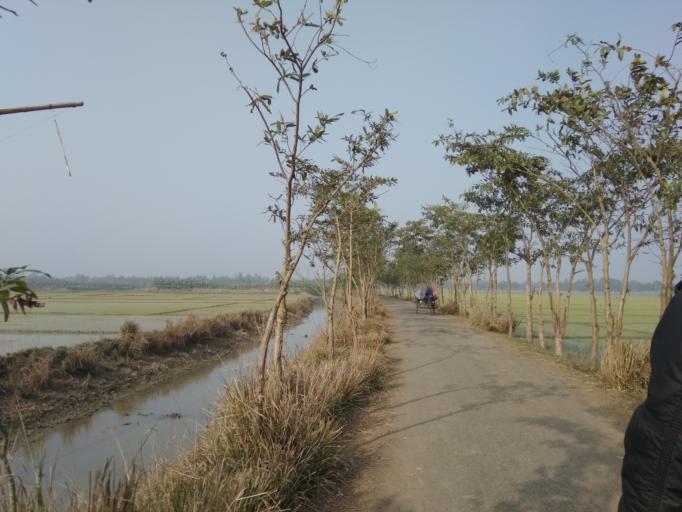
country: BD
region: Rajshahi
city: Bogra
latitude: 24.4702
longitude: 89.2682
